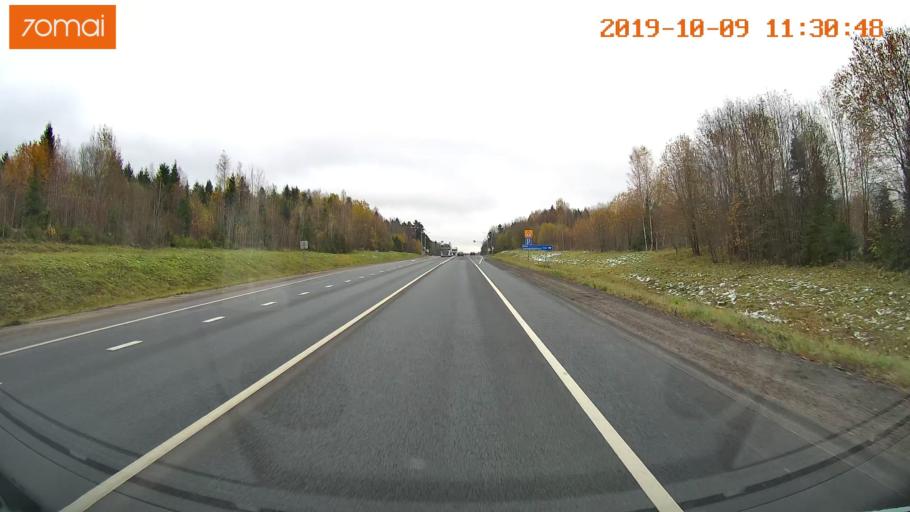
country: RU
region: Vologda
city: Gryazovets
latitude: 59.0508
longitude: 40.0828
